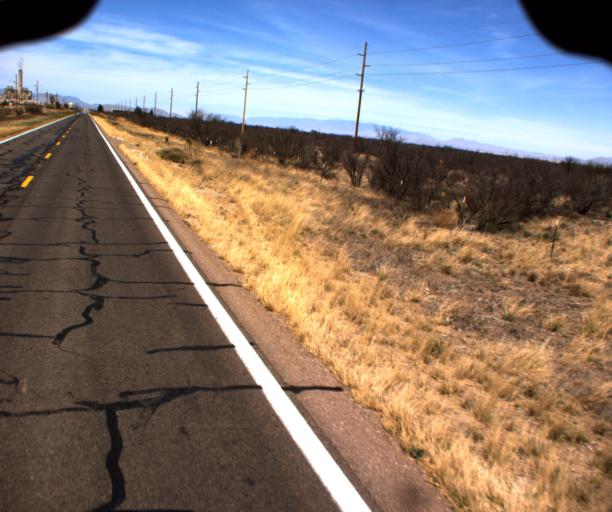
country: US
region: Arizona
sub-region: Cochise County
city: Willcox
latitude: 32.0427
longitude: -109.8823
